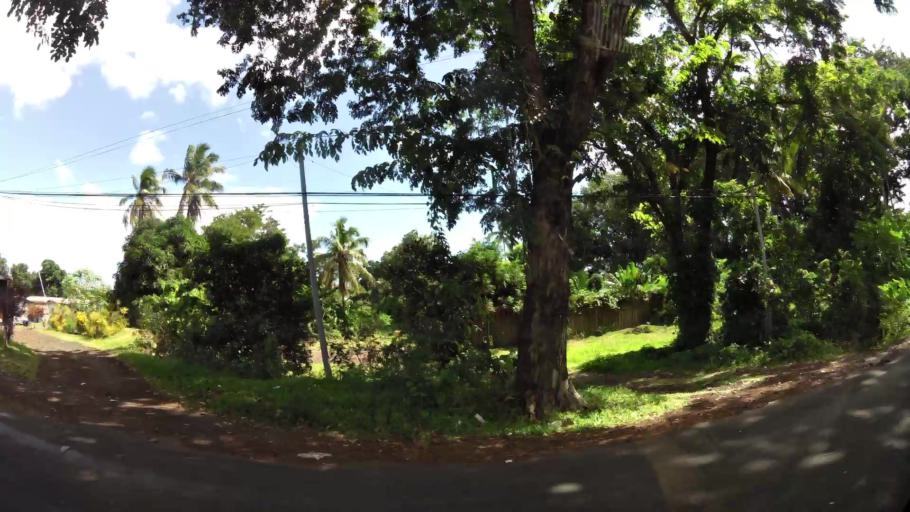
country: KM
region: Grande Comore
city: Mavingouni
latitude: -11.7320
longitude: 43.2501
